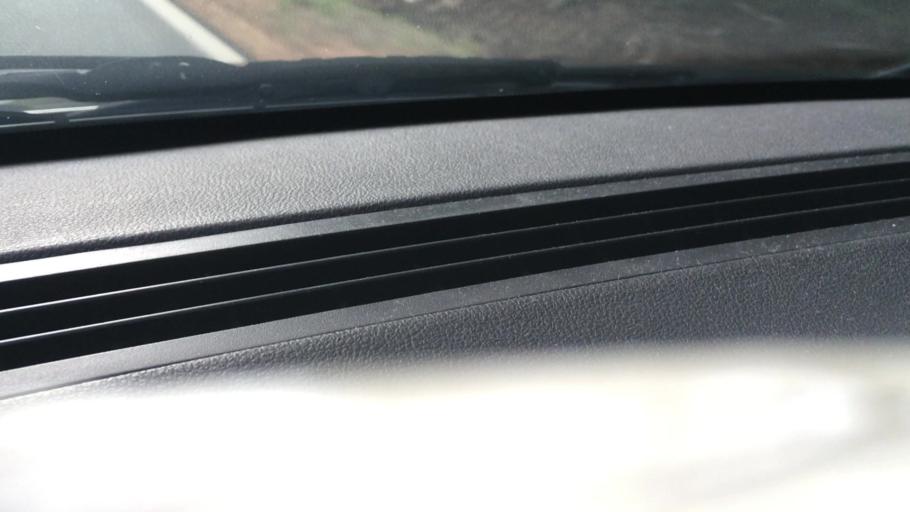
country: US
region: Alabama
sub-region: Shelby County
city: Helena
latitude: 33.2548
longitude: -86.9425
